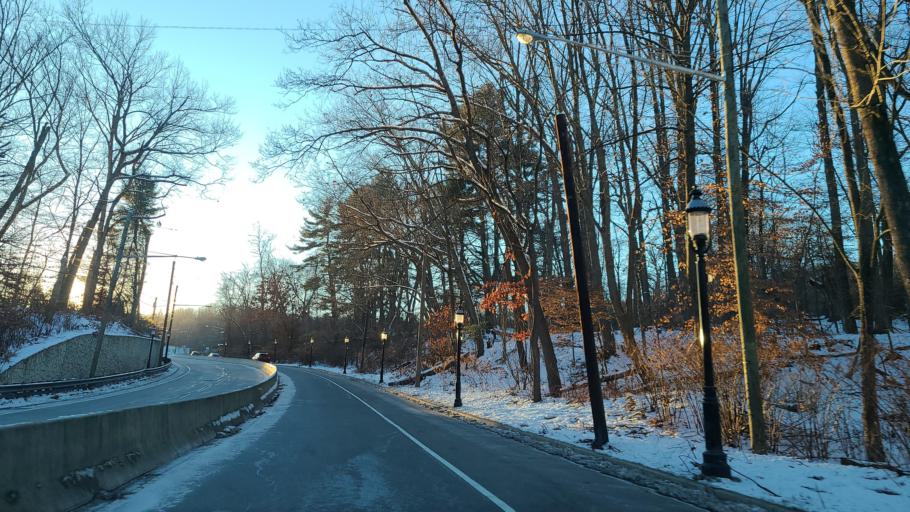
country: US
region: New Jersey
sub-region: Essex County
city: Maplewood
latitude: 40.7538
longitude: -74.2926
